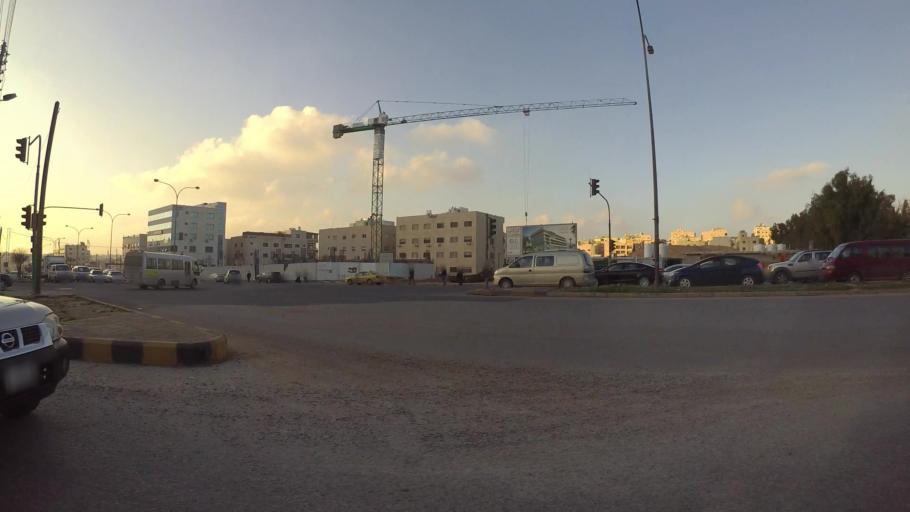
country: JO
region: Amman
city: Al Bunayyat ash Shamaliyah
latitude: 31.9137
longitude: 35.9159
